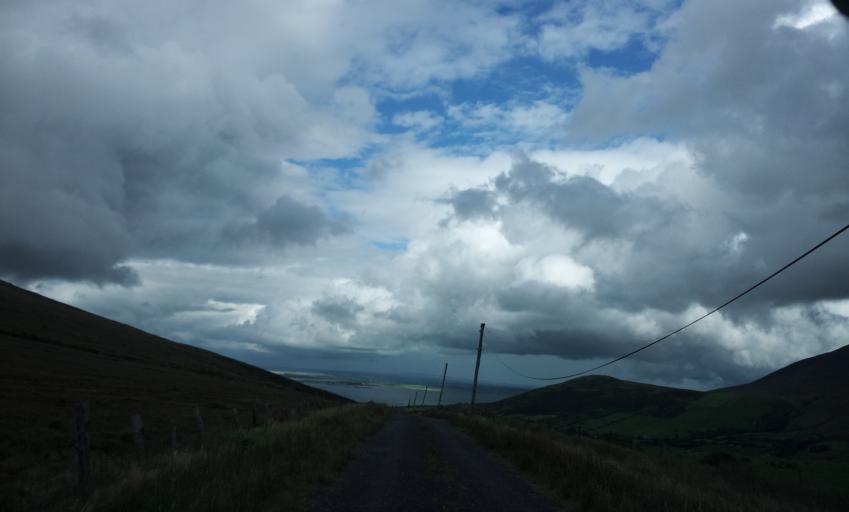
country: IE
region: Munster
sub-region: Ciarrai
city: Killorglin
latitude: 52.1972
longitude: -9.9209
